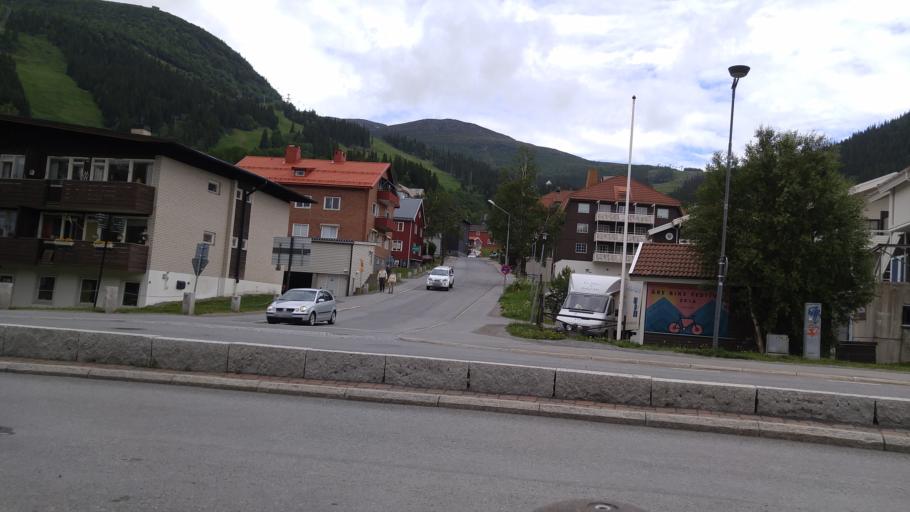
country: SE
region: Jaemtland
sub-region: Are Kommun
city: Are
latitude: 63.3987
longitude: 13.0771
